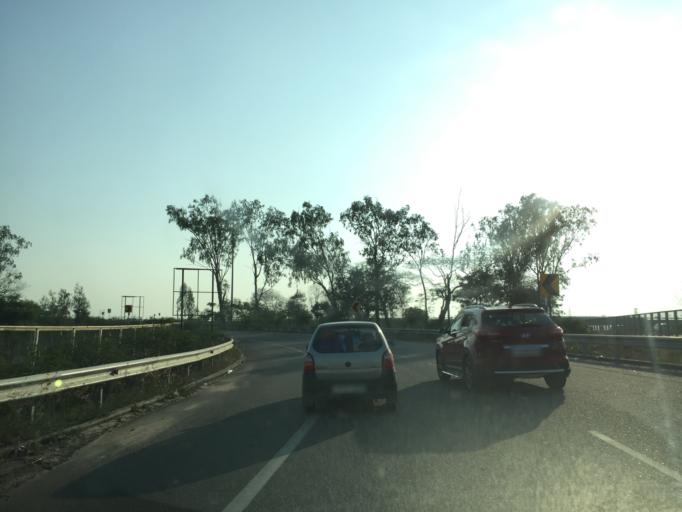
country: IN
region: Telangana
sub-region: Rangareddi
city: Ghatkesar
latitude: 17.4407
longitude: 78.6690
